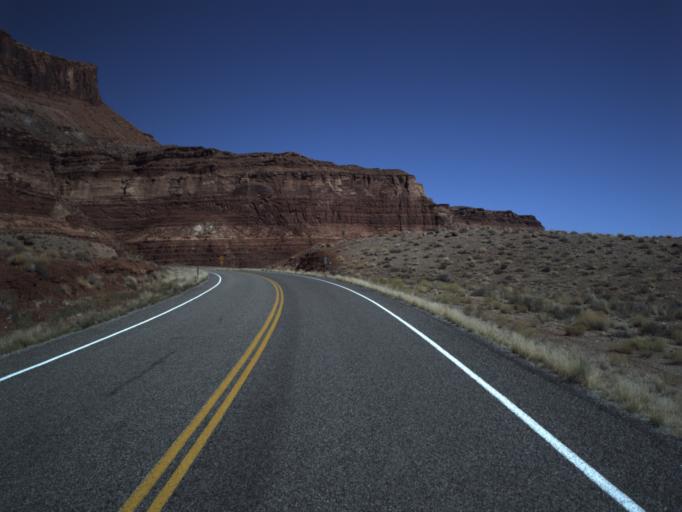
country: US
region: Utah
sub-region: San Juan County
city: Blanding
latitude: 37.9135
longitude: -110.3981
